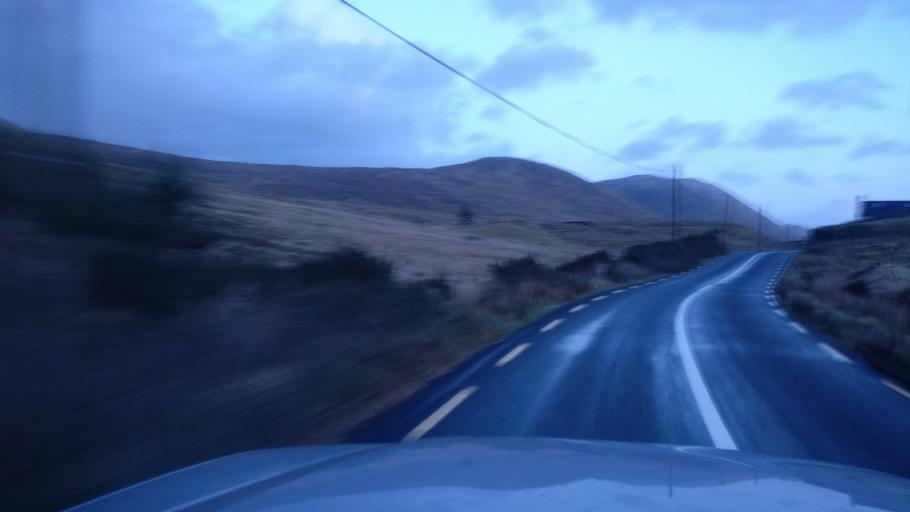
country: IE
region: Connaught
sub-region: Maigh Eo
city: Westport
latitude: 53.5854
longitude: -9.6811
